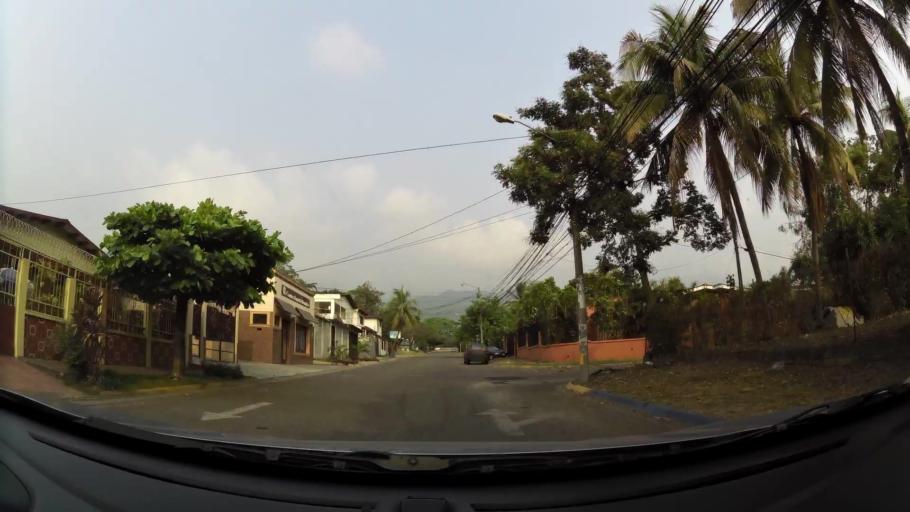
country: HN
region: Cortes
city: Armenta
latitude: 15.4869
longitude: -88.0358
